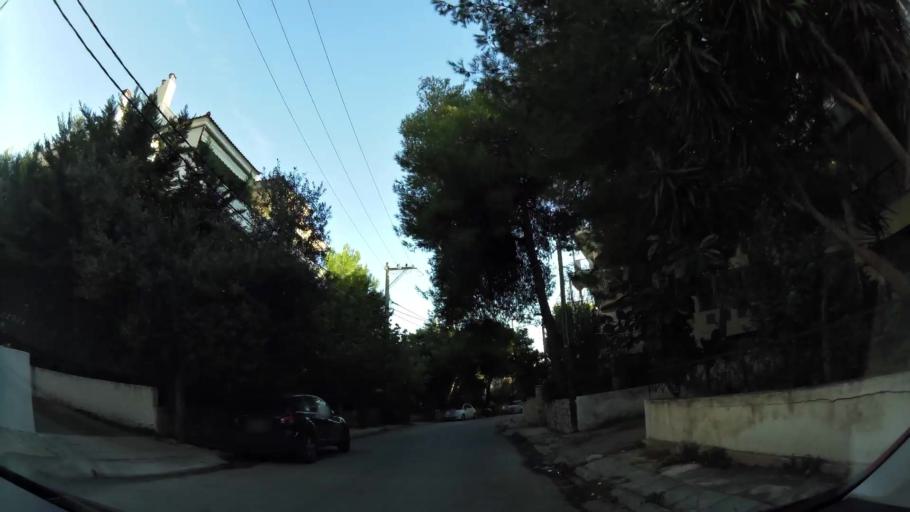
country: GR
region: Attica
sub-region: Nomarchia Anatolikis Attikis
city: Rafina
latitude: 38.0093
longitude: 24.0172
